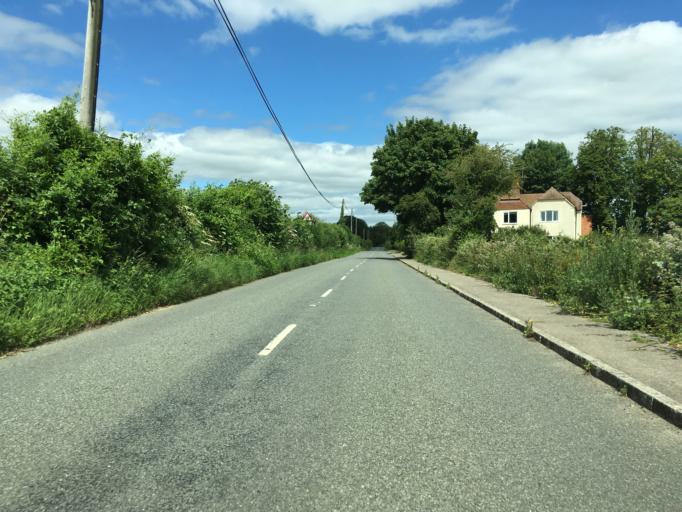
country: GB
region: England
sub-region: West Berkshire
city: Welford
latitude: 51.4421
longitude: -1.3931
